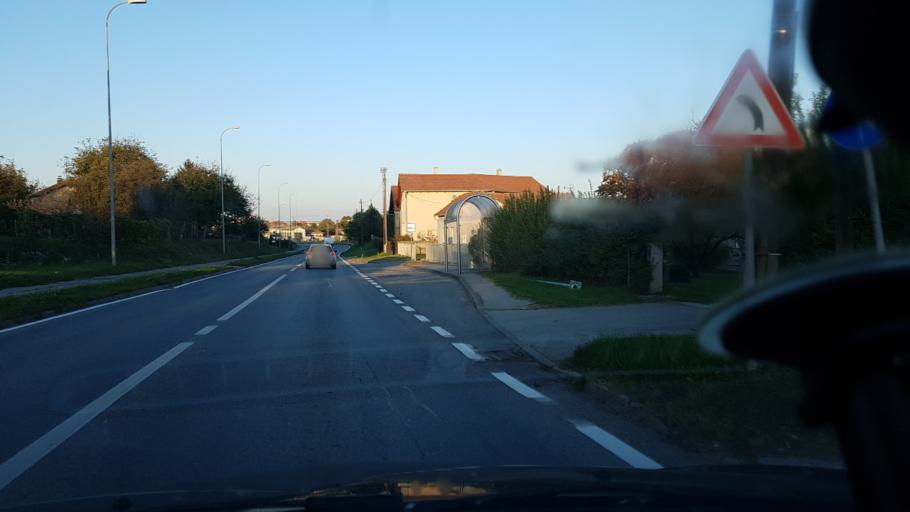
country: HR
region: Koprivnicko-Krizevacka
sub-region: Grad Koprivnica
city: Koprivnica
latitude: 46.1581
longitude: 16.8094
